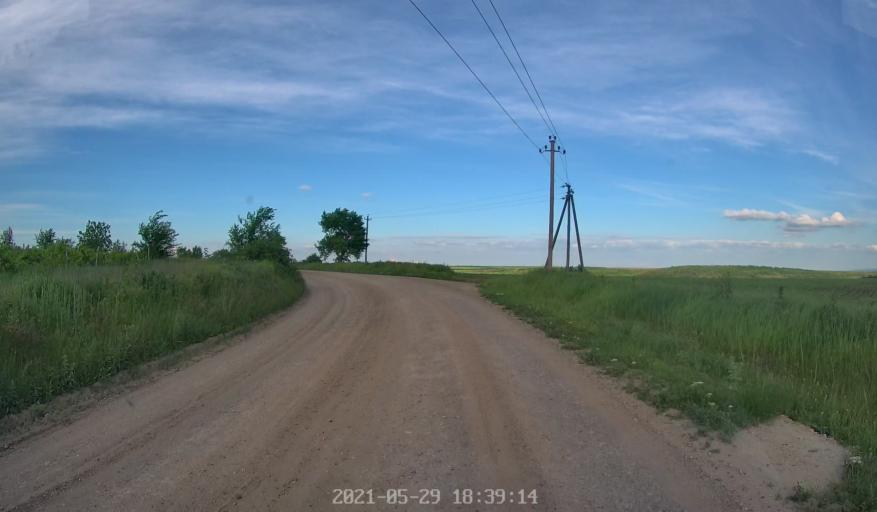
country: MD
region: Chisinau
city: Singera
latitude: 46.8008
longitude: 28.9430
